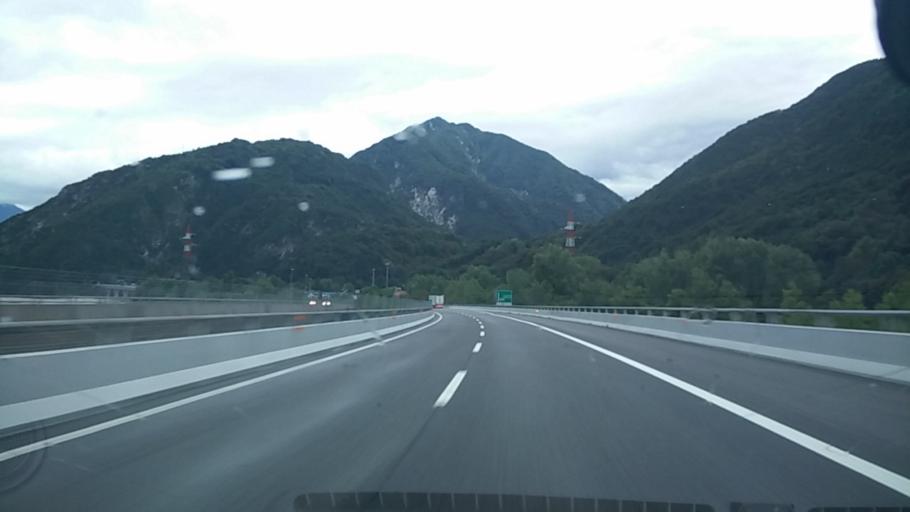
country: IT
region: Friuli Venezia Giulia
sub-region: Provincia di Udine
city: Moggio di Sotto
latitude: 46.3988
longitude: 13.1749
